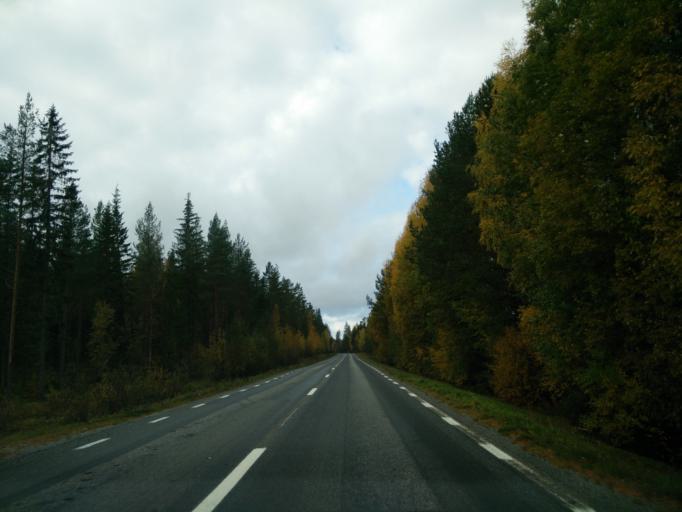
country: SE
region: Jaemtland
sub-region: Braecke Kommun
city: Braecke
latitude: 62.4031
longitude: 15.2591
